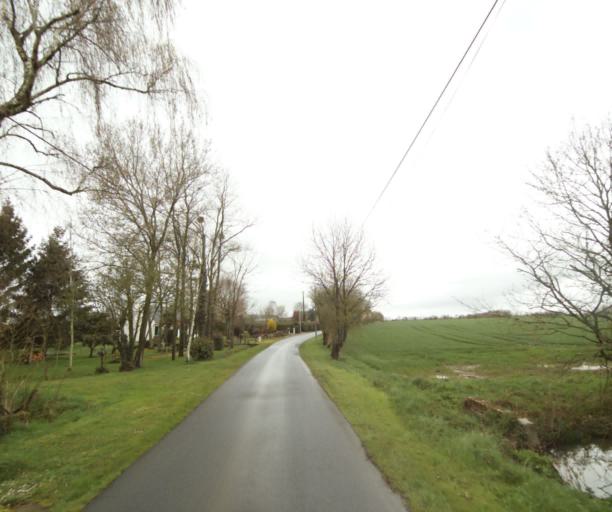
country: FR
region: Pays de la Loire
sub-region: Departement de la Loire-Atlantique
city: Bouvron
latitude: 47.4454
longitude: -1.8780
